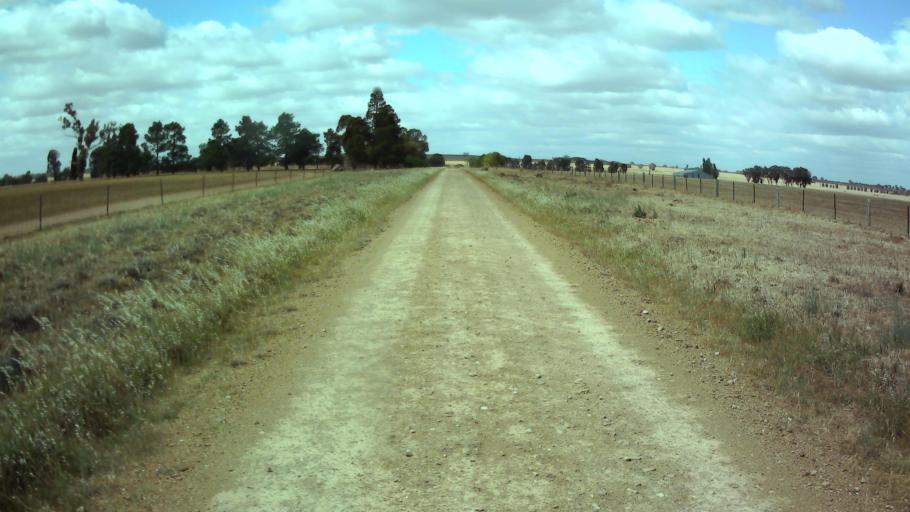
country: AU
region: New South Wales
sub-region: Weddin
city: Grenfell
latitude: -34.0579
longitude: 148.3308
